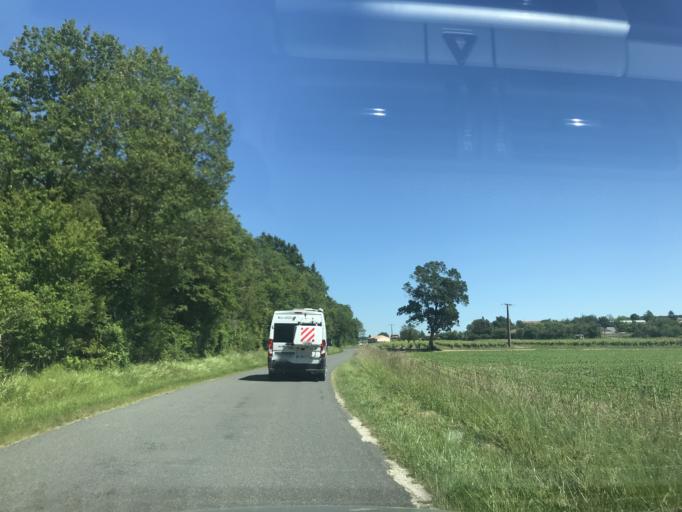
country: FR
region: Poitou-Charentes
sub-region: Departement de la Charente-Maritime
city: Mortagne-sur-Gironde
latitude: 45.4231
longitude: -0.7173
